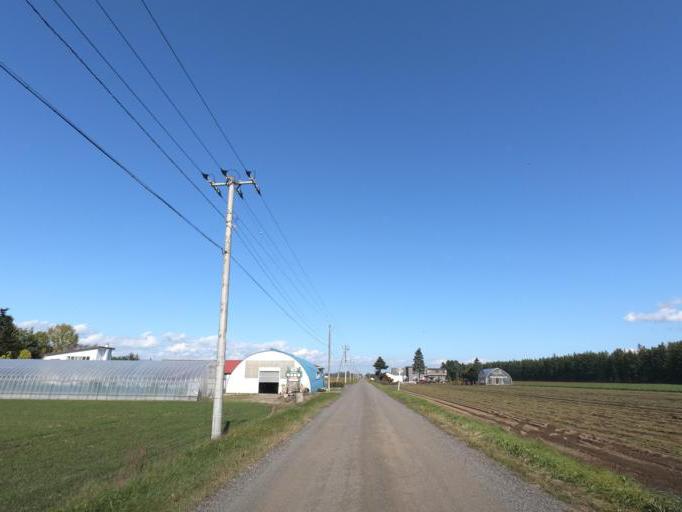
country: JP
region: Hokkaido
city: Otofuke
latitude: 43.0768
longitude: 143.2600
